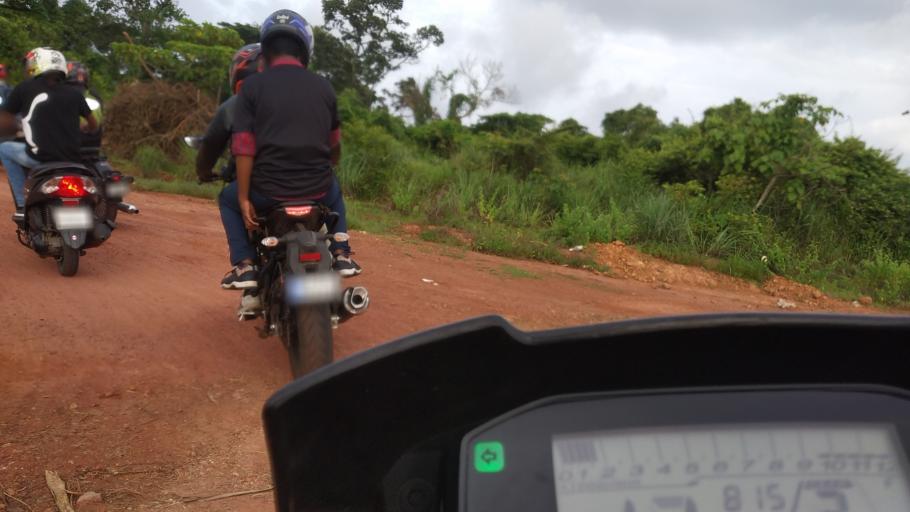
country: IN
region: Kerala
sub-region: Ernakulam
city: Aluva
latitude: 10.0528
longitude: 76.3441
